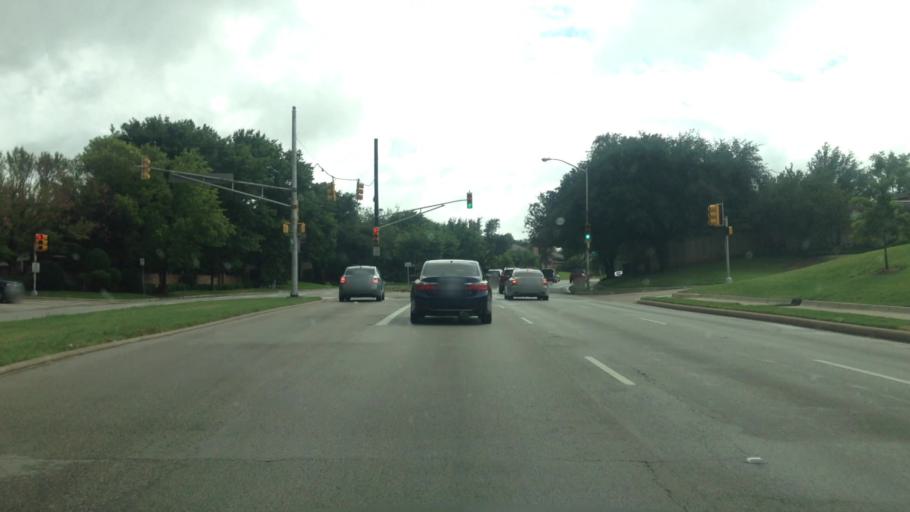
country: US
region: Texas
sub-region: Tarrant County
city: Edgecliff Village
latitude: 32.6966
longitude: -97.3910
